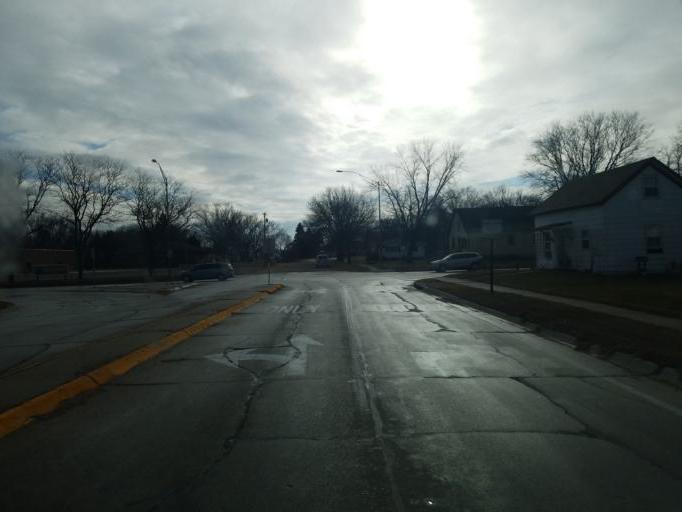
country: US
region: Nebraska
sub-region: Pierce County
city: Pierce
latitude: 42.1967
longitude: -97.5286
